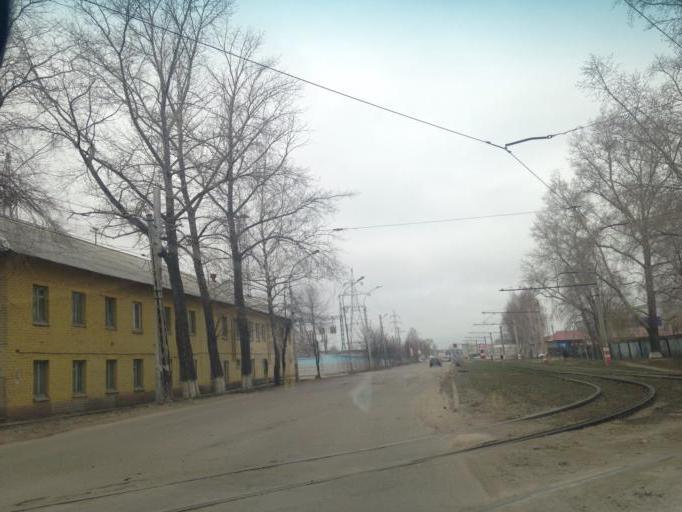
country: RU
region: Ulyanovsk
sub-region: Ulyanovskiy Rayon
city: Ulyanovsk
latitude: 54.2924
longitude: 48.2939
